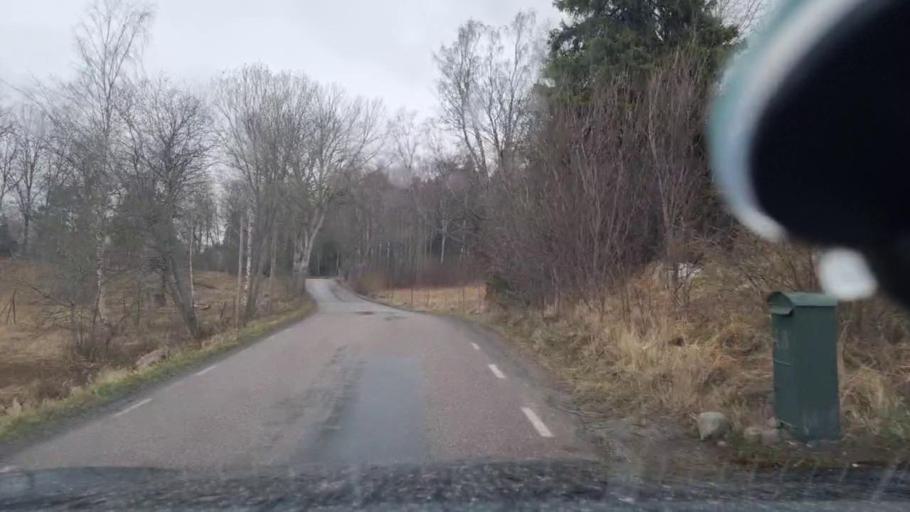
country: SE
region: Stockholm
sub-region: Taby Kommun
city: Taby
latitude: 59.4845
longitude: 18.0141
